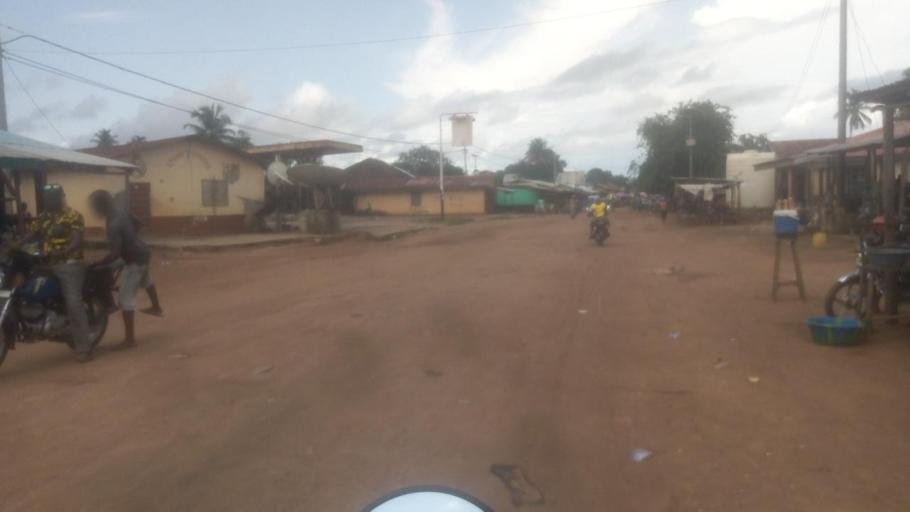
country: SL
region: Northern Province
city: Tintafor
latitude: 8.6291
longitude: -13.2178
